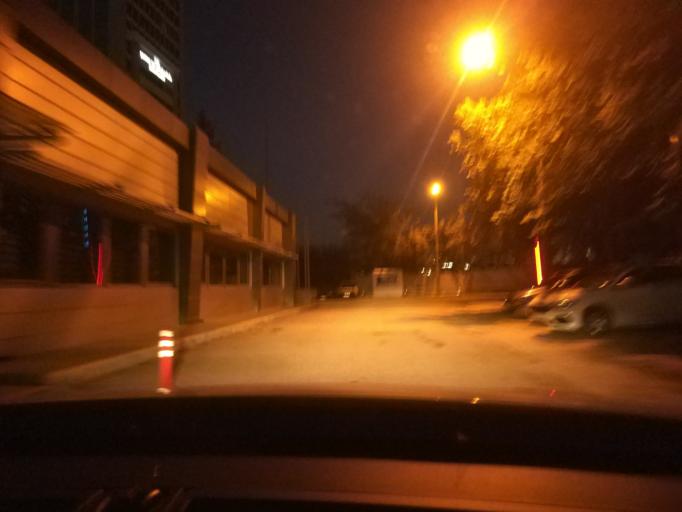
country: TR
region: Ankara
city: Batikent
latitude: 39.9106
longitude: 32.7505
